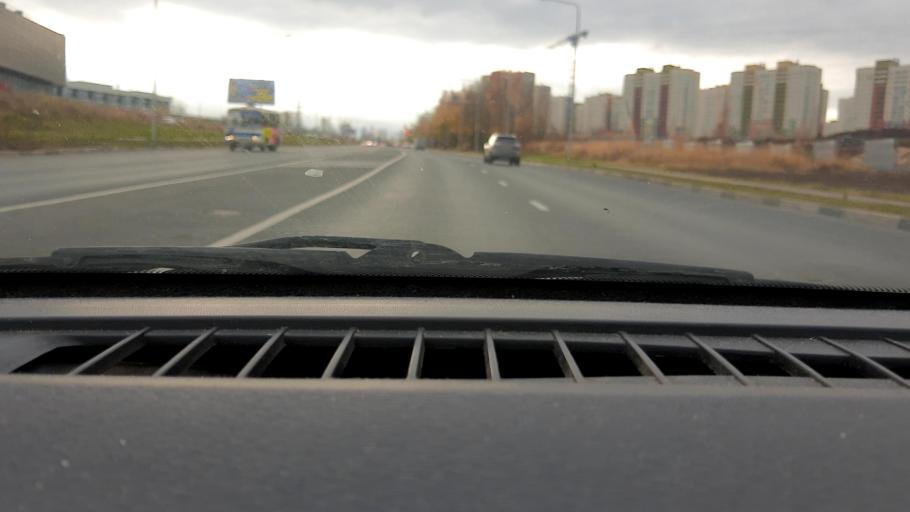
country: RU
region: Nizjnij Novgorod
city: Nizhniy Novgorod
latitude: 56.2698
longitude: 44.0230
